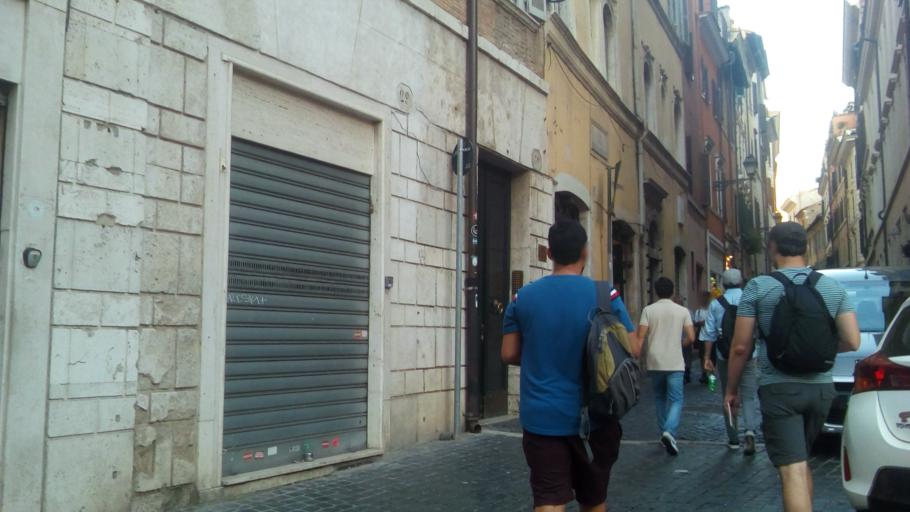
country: VA
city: Vatican City
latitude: 41.9004
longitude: 12.4670
